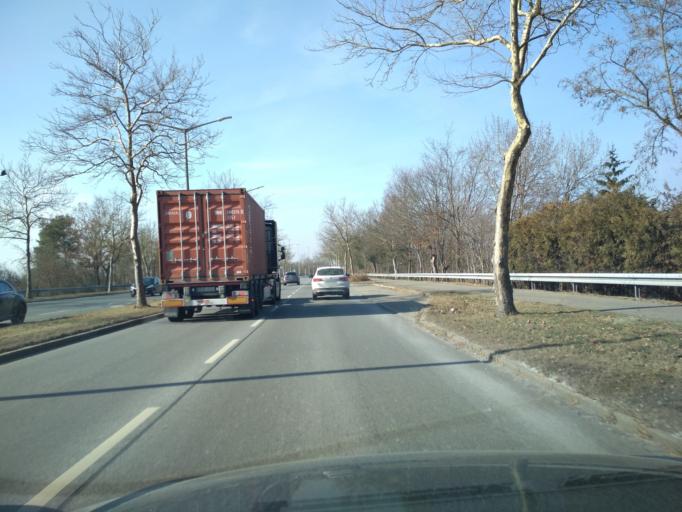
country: DE
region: Bavaria
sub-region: Regierungsbezirk Mittelfranken
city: Stein
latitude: 49.4065
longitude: 11.0572
